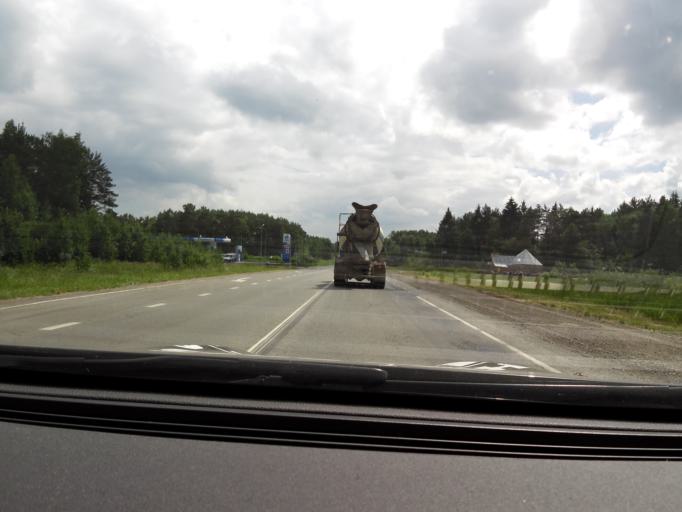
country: RU
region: Perm
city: Kungur
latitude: 57.3111
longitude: 56.9747
